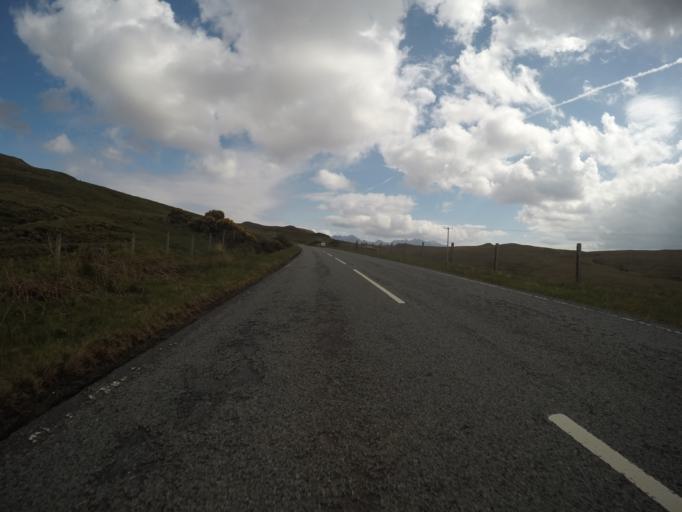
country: GB
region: Scotland
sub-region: Highland
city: Isle of Skye
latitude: 57.3216
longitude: -6.3277
